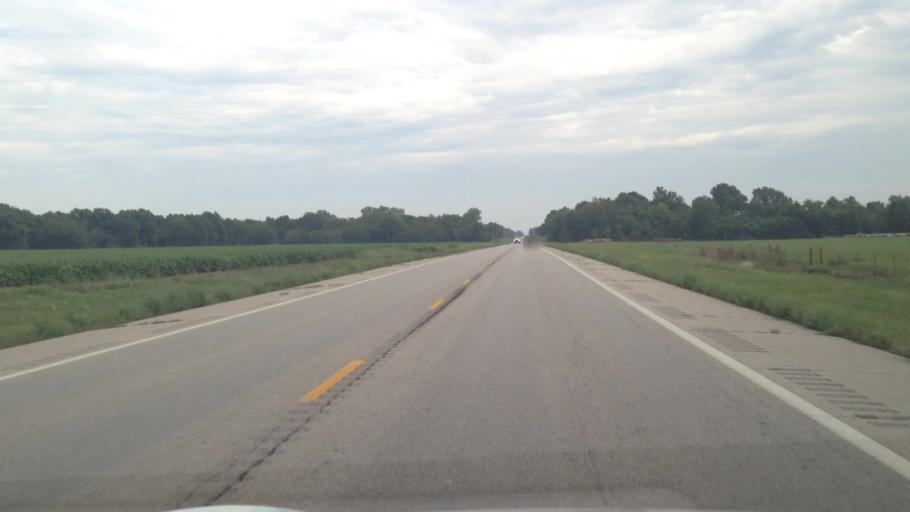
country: US
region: Kansas
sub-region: Crawford County
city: Pittsburg
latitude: 37.3392
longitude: -94.7911
